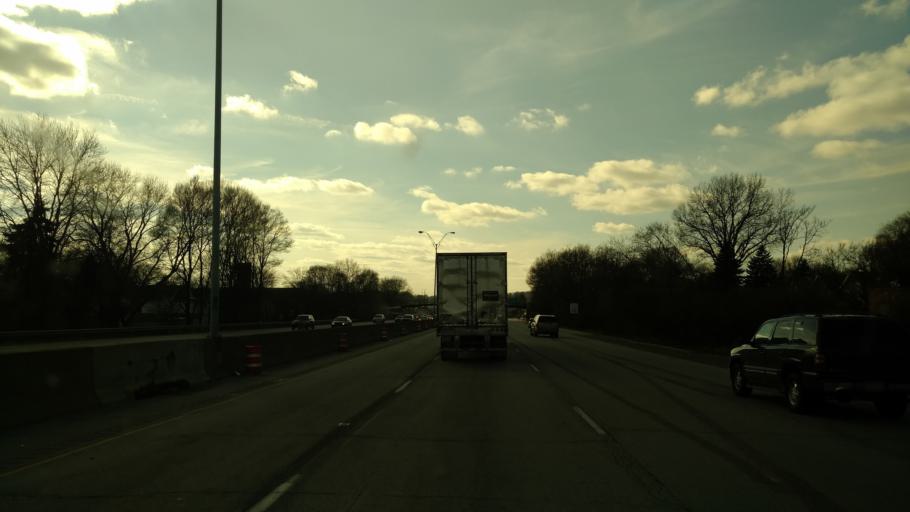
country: US
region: Ohio
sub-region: Summit County
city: Akron
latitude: 41.0625
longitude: -81.5113
